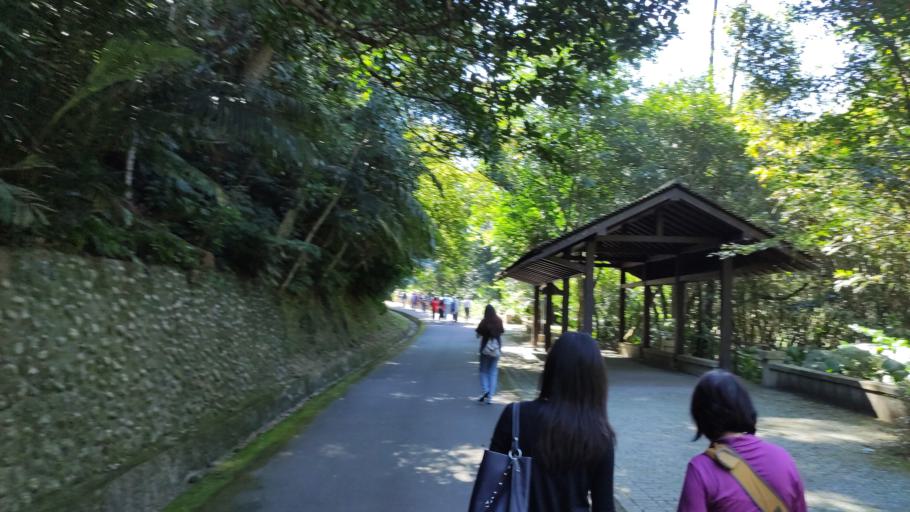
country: TW
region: Taiwan
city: Daxi
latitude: 24.8419
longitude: 121.3072
